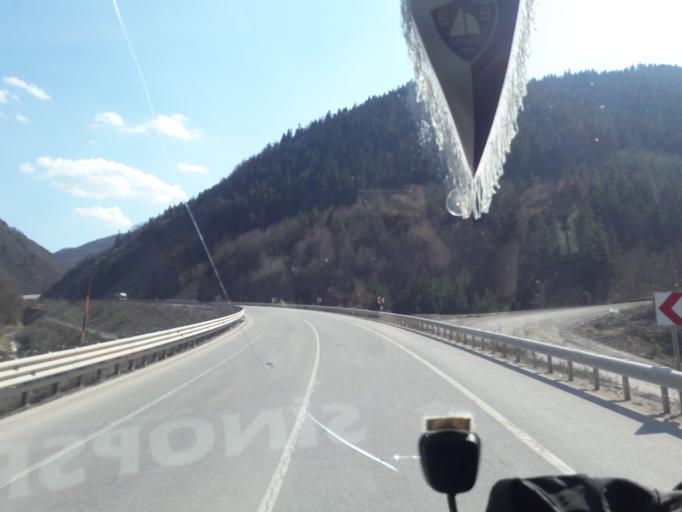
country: TR
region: Sinop
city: Erfelek
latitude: 41.6957
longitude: 34.9092
